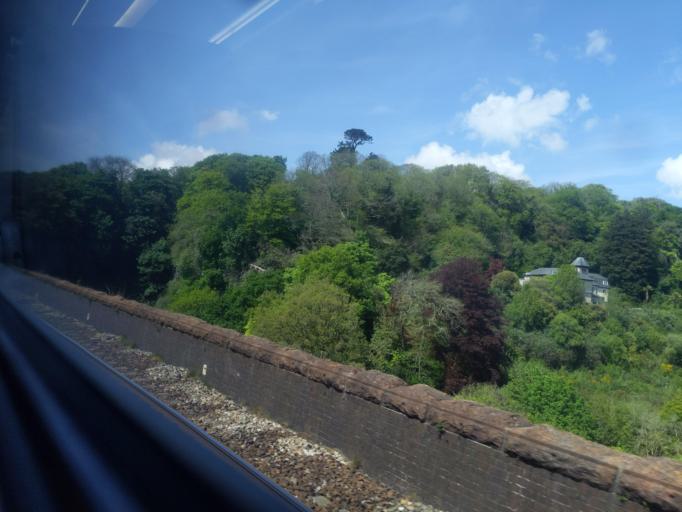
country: GB
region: England
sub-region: Cornwall
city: St Austell
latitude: 50.3424
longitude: -4.7978
